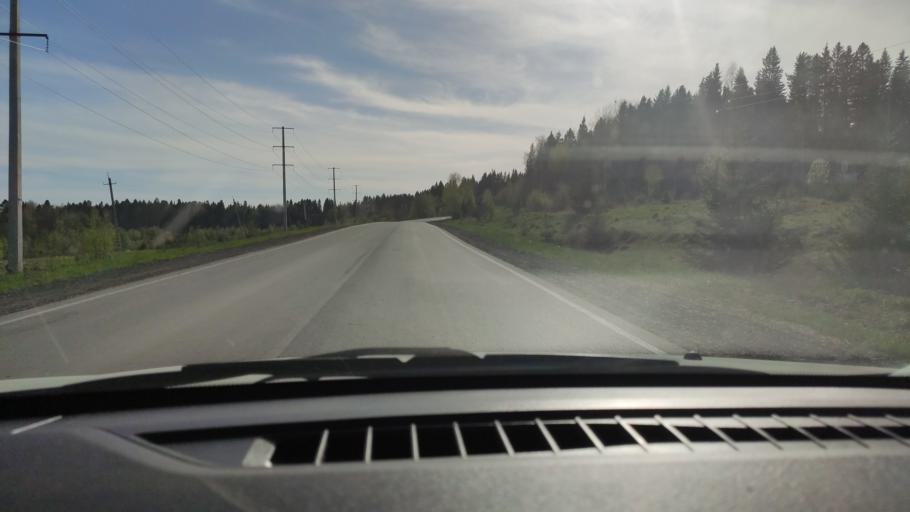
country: RU
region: Perm
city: Novyye Lyady
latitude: 57.9198
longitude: 56.6669
